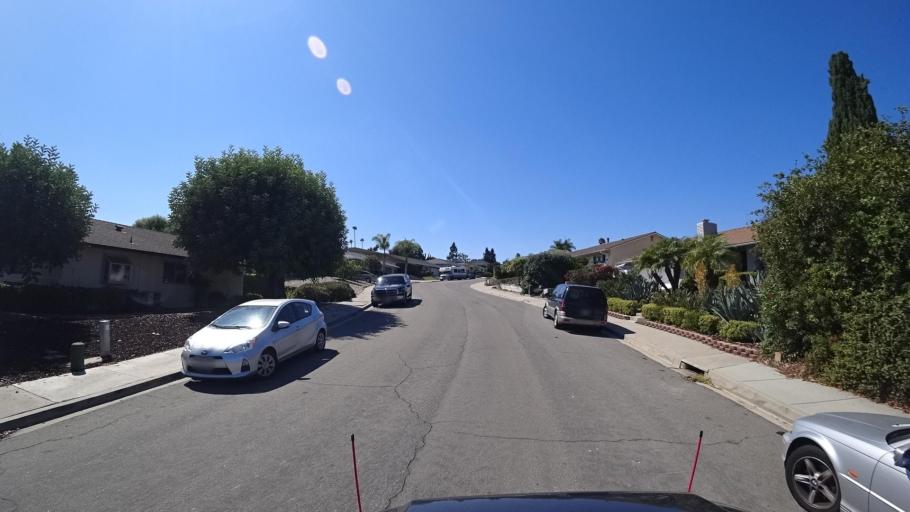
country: US
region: California
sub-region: San Diego County
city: Lake San Marcos
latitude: 33.1265
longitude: -117.2097
